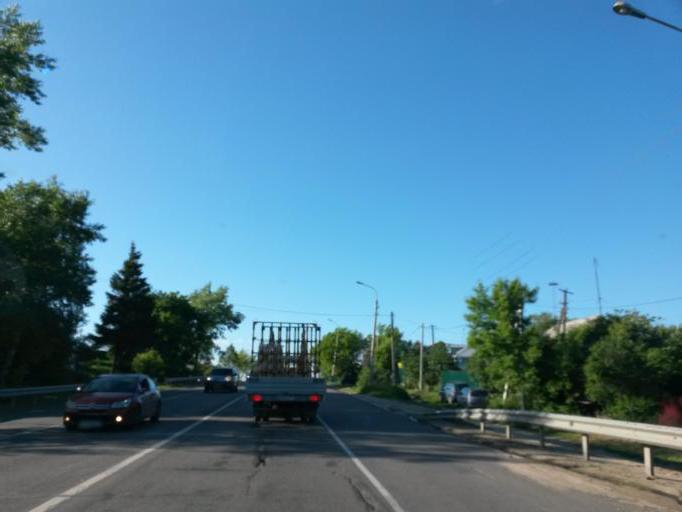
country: RU
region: Moskovskaya
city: Stolbovaya
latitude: 55.2762
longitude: 37.5099
